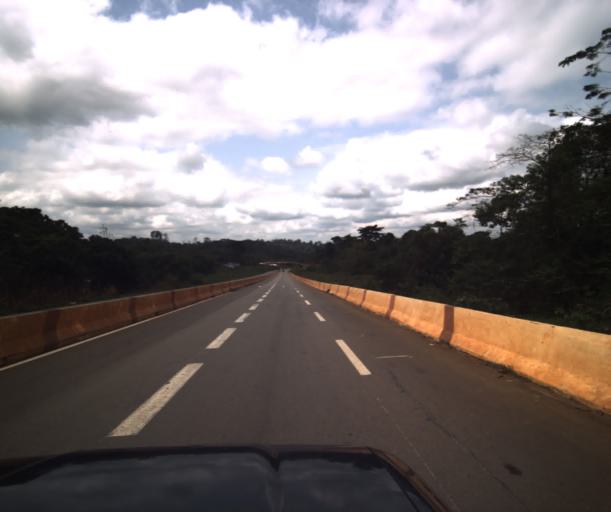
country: CM
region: Centre
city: Mbankomo
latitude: 3.7988
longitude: 11.3347
